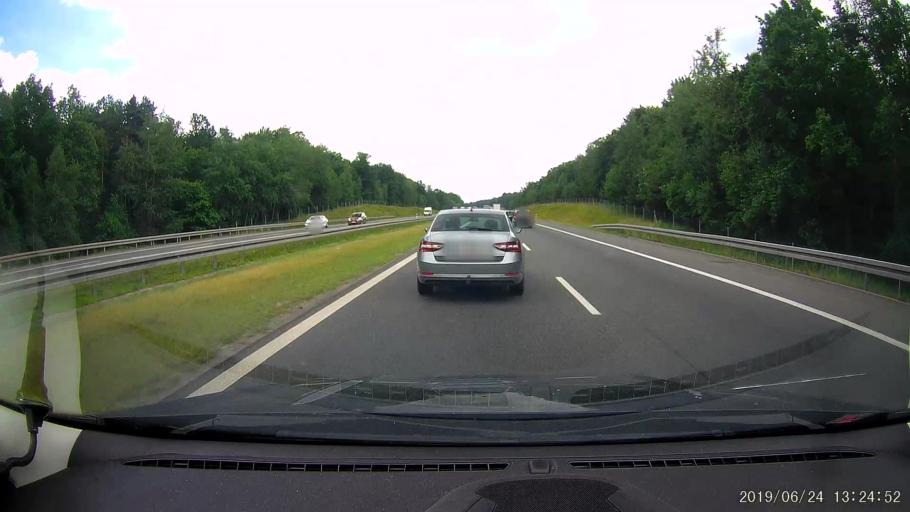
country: PL
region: Silesian Voivodeship
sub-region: Katowice
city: Murcki
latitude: 50.2245
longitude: 19.0867
